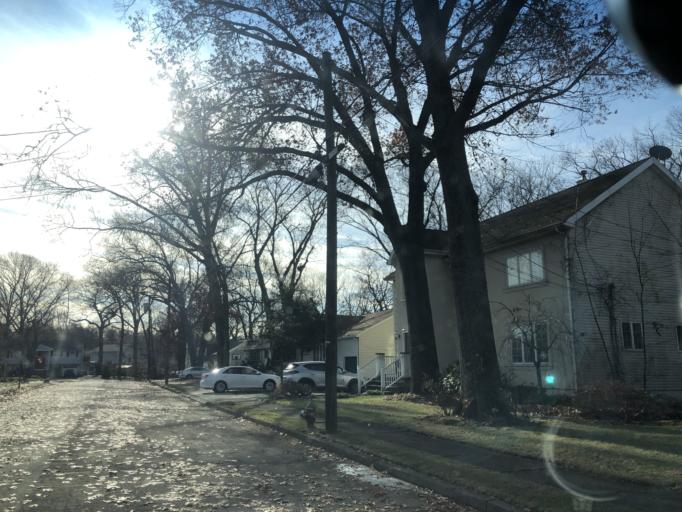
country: US
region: New Jersey
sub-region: Bergen County
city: Fair Lawn
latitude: 40.9265
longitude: -74.1407
